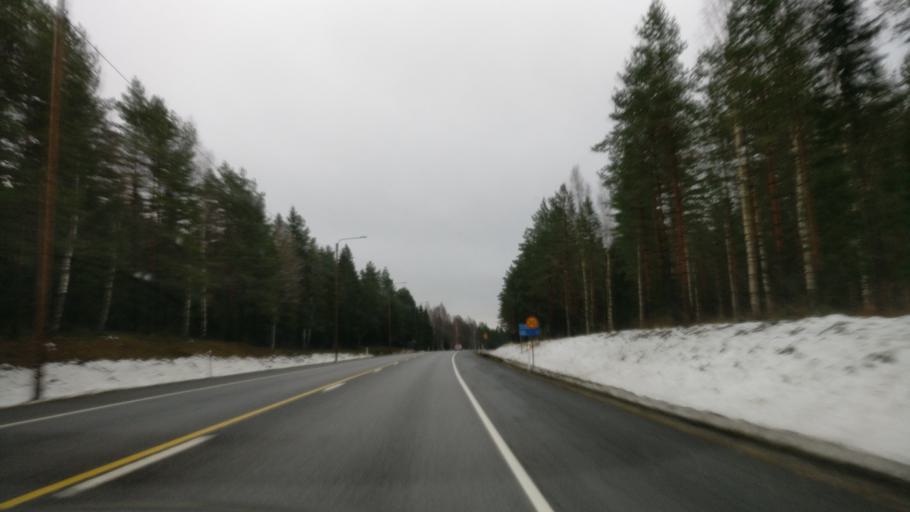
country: FI
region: Uusimaa
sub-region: Raaseporin
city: Karis
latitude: 60.0672
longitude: 23.8144
